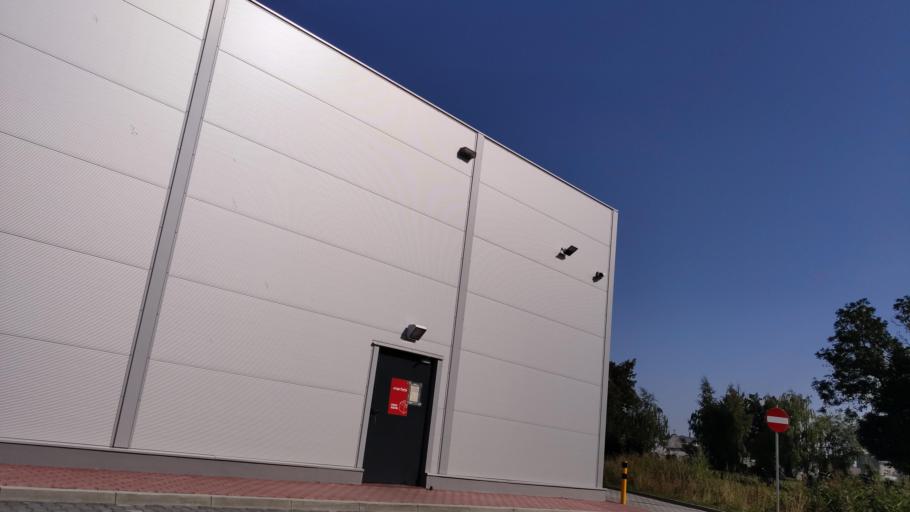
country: PL
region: Kujawsko-Pomorskie
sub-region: Powiat zninski
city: Znin
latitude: 52.8466
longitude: 17.7348
